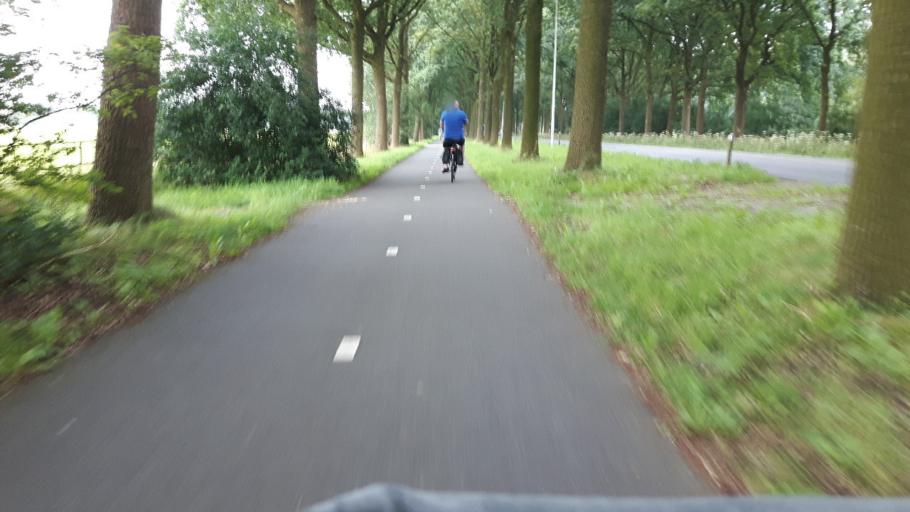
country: NL
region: Utrecht
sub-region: Gemeente Zeist
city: Zeist
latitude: 52.0722
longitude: 5.2246
